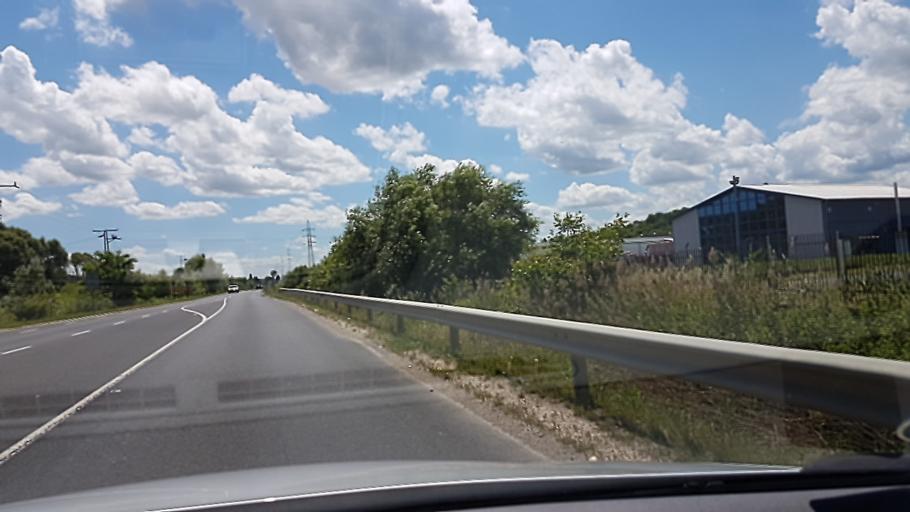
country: HU
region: Zala
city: Zalaegerszeg
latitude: 46.8413
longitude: 16.8650
